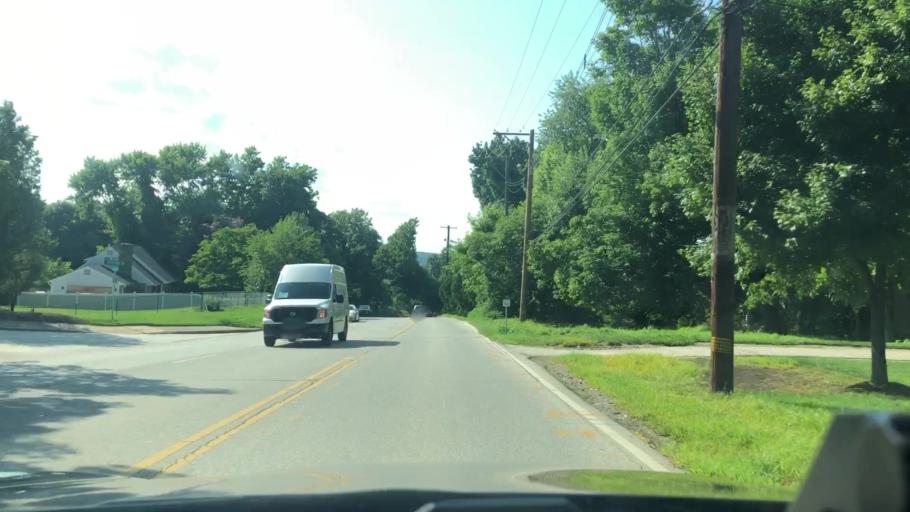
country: US
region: Pennsylvania
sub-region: Montgomery County
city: Wyndmoor
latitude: 40.0952
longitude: -75.1932
